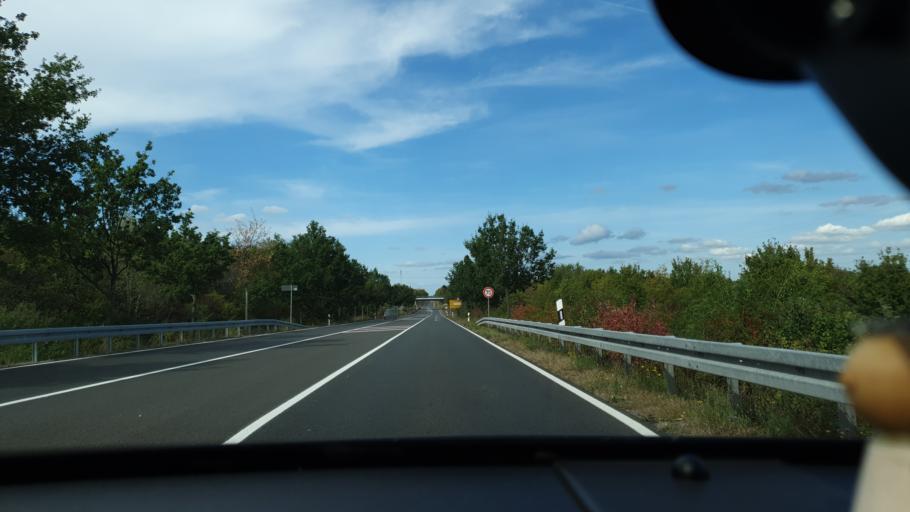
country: DE
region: Saxony
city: Eilenburg
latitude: 51.4469
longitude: 12.6134
